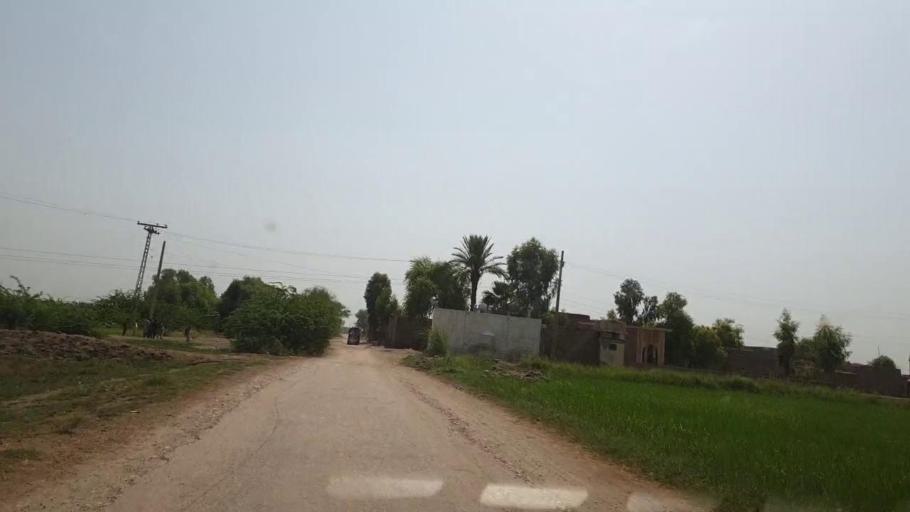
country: PK
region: Sindh
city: Lakhi
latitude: 27.8803
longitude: 68.6790
